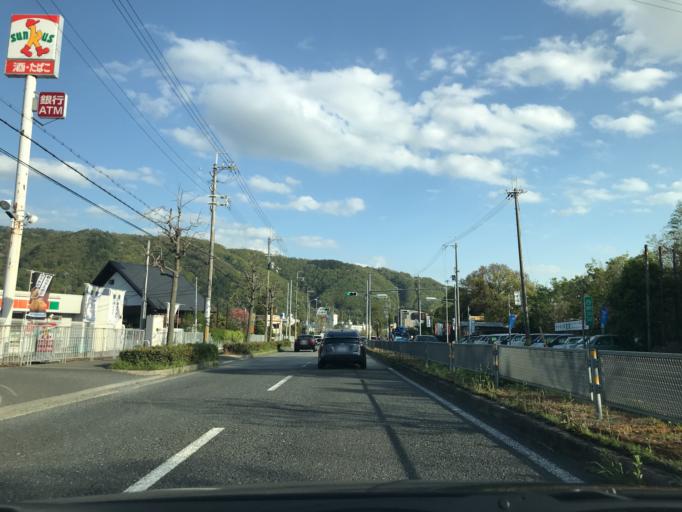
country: JP
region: Osaka
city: Ikeda
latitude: 34.8470
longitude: 135.4214
